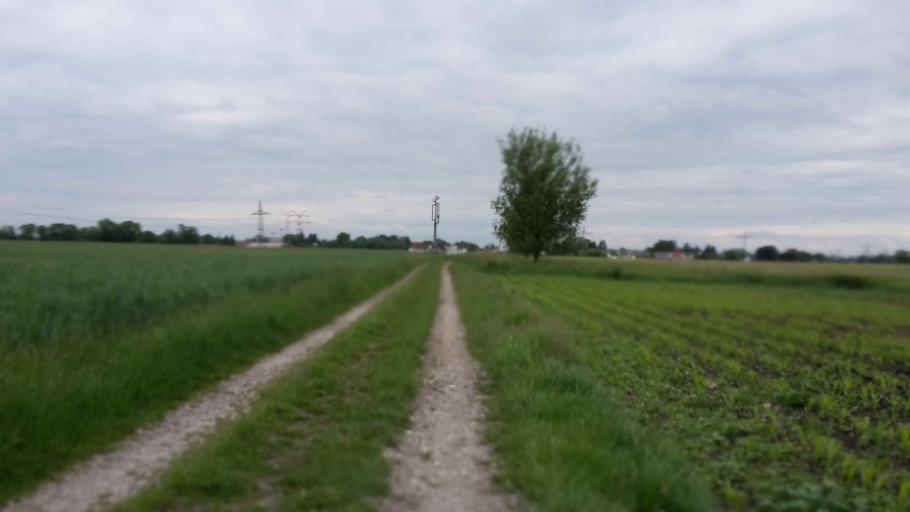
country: DE
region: Bavaria
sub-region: Upper Bavaria
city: Grobenzell
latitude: 48.1904
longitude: 11.4143
